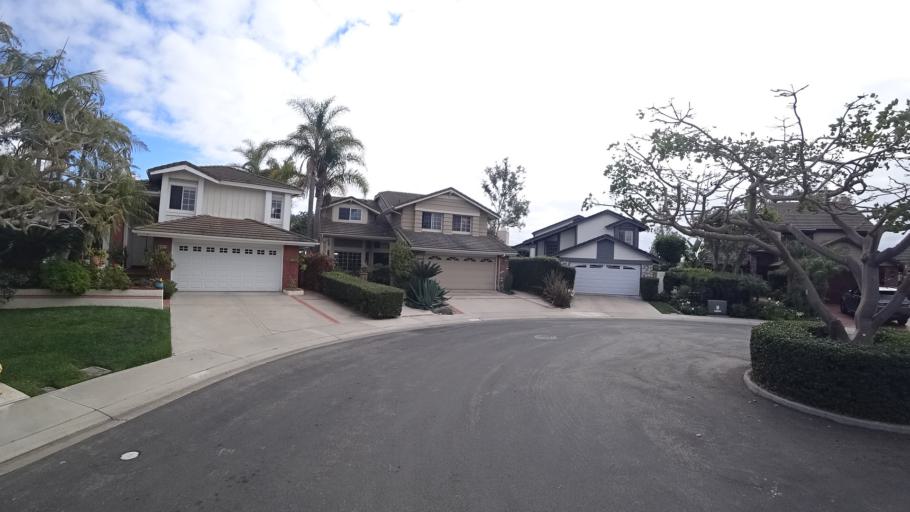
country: US
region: California
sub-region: Orange County
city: Dana Point
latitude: 33.4841
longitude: -117.6955
